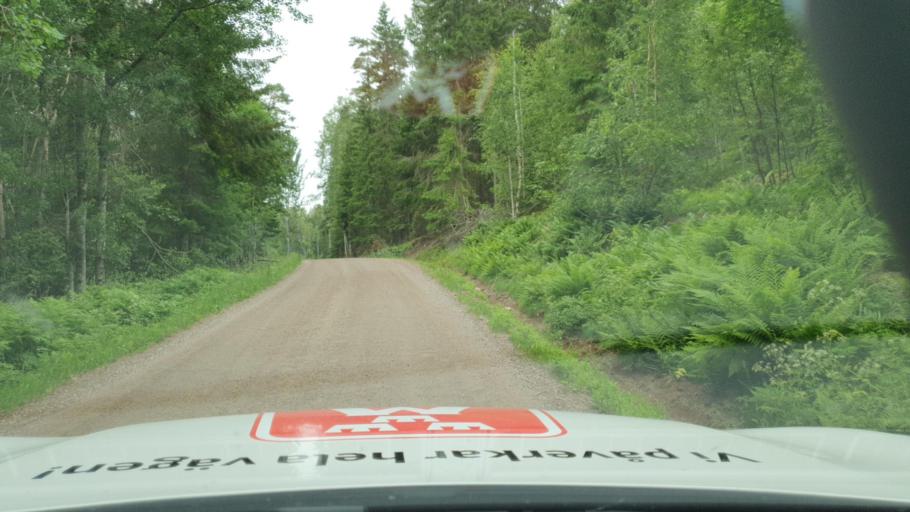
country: SE
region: Vaermland
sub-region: Filipstads Kommun
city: Filipstad
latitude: 59.5811
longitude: 13.9551
